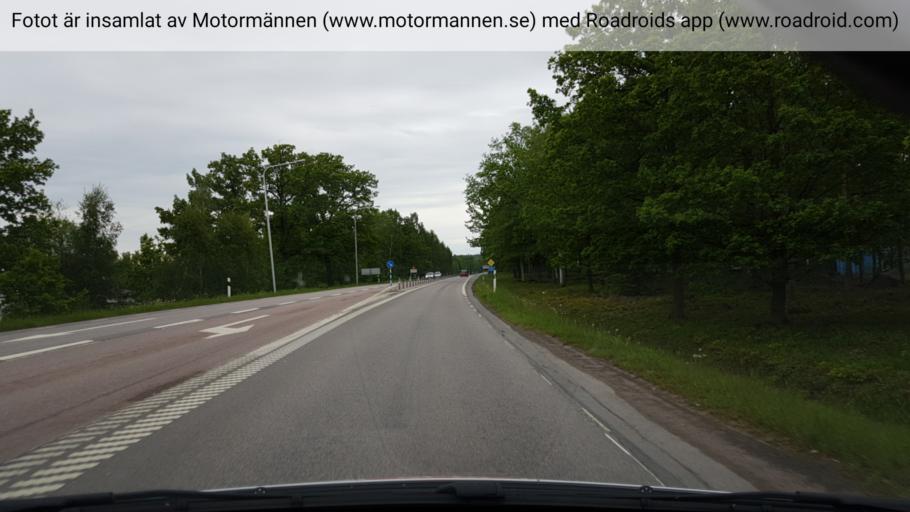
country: SE
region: OEstergoetland
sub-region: Motala Kommun
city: Motala
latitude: 58.5585
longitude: 15.0623
